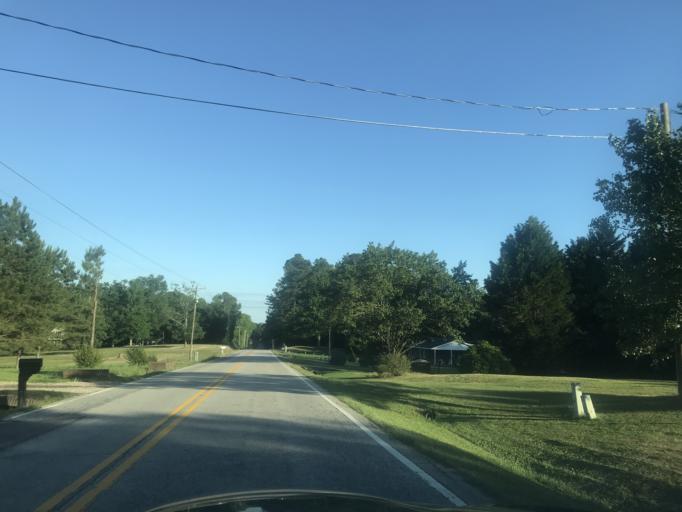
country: US
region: North Carolina
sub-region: Johnston County
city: Archer Lodge
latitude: 35.7262
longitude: -78.3879
